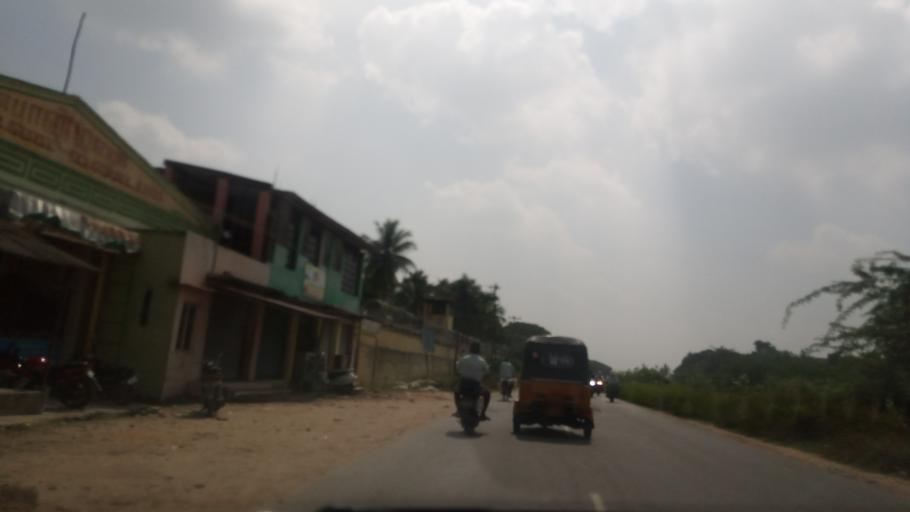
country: IN
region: Tamil Nadu
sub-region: Vellore
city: Arakkonam
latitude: 13.0706
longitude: 79.6724
